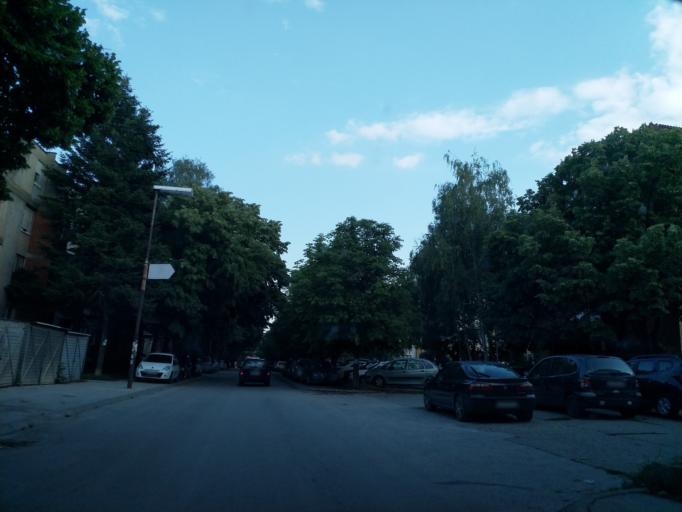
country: RS
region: Central Serbia
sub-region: Pomoravski Okrug
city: Jagodina
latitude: 43.9792
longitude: 21.2470
